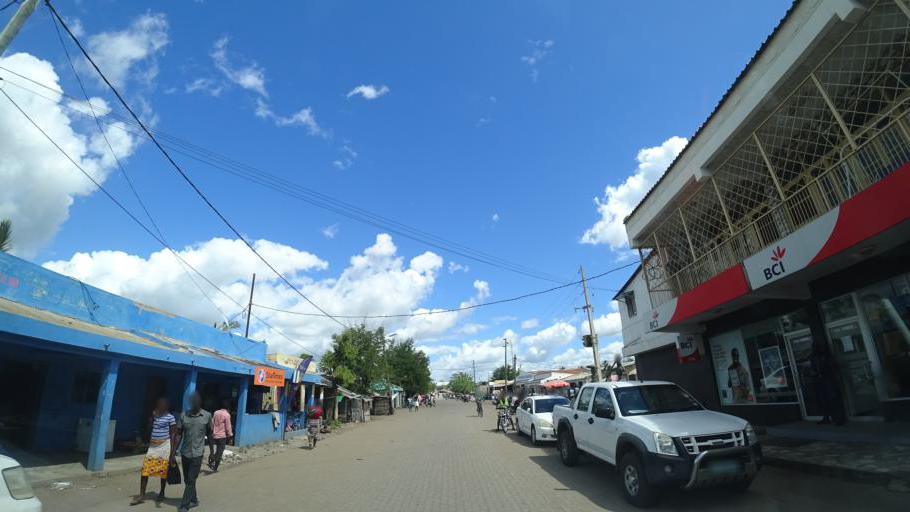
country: MZ
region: Sofala
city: Dondo
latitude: -19.2709
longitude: 34.2081
